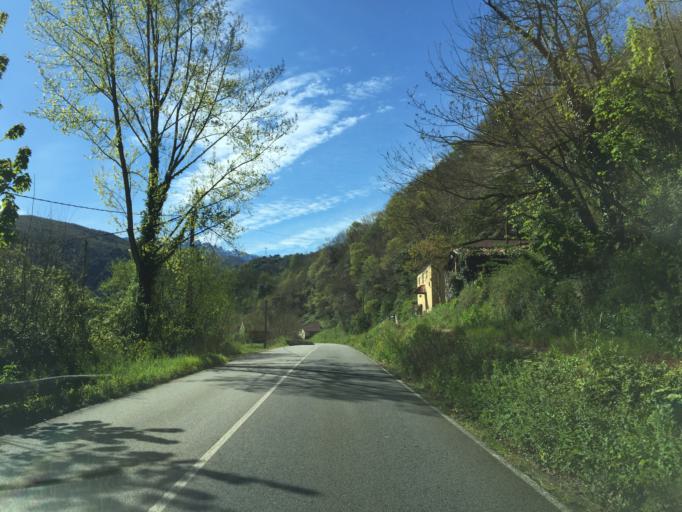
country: ES
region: Asturias
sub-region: Province of Asturias
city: Proaza
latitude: 43.3174
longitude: -5.9918
